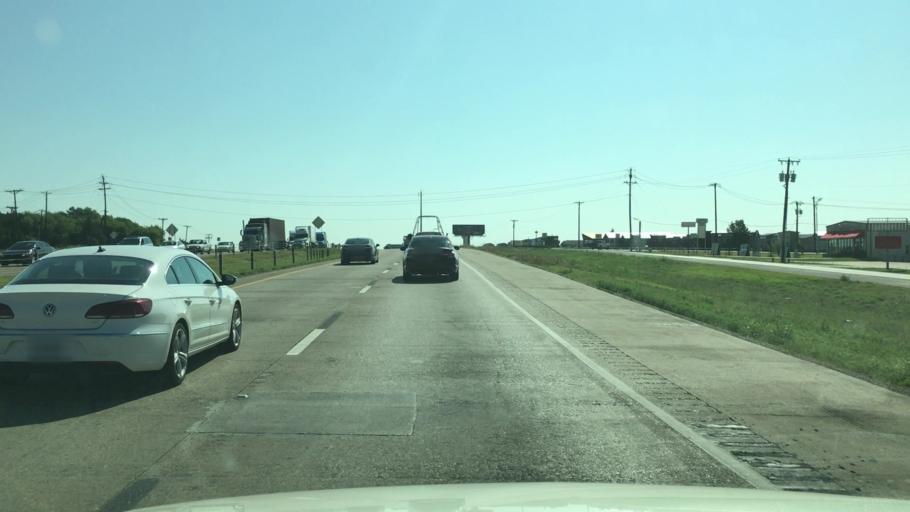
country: US
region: Texas
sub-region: Rockwall County
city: Fate
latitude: 32.9233
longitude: -96.4028
